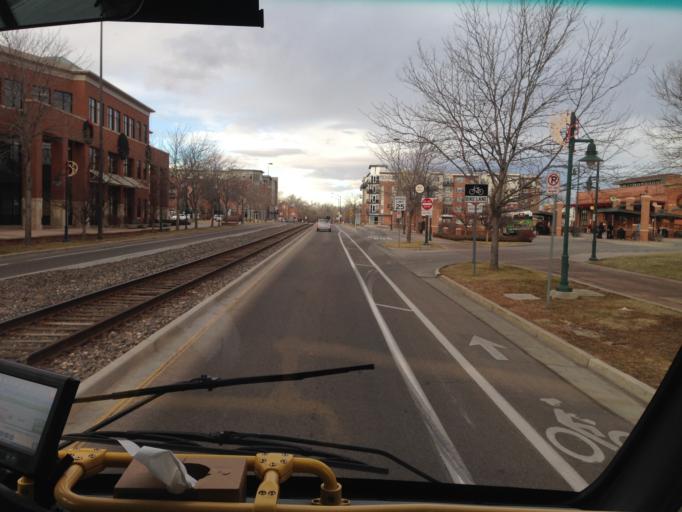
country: US
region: Colorado
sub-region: Larimer County
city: Fort Collins
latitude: 40.5890
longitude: -105.0789
